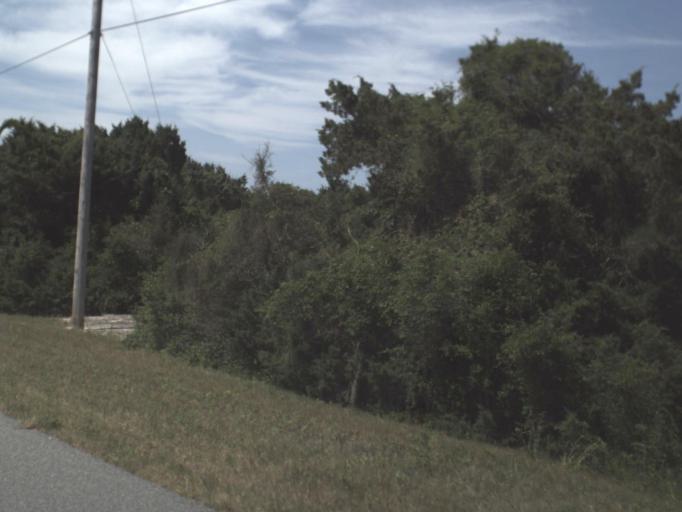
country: US
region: Florida
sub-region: Duval County
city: Atlantic Beach
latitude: 30.4563
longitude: -81.4168
